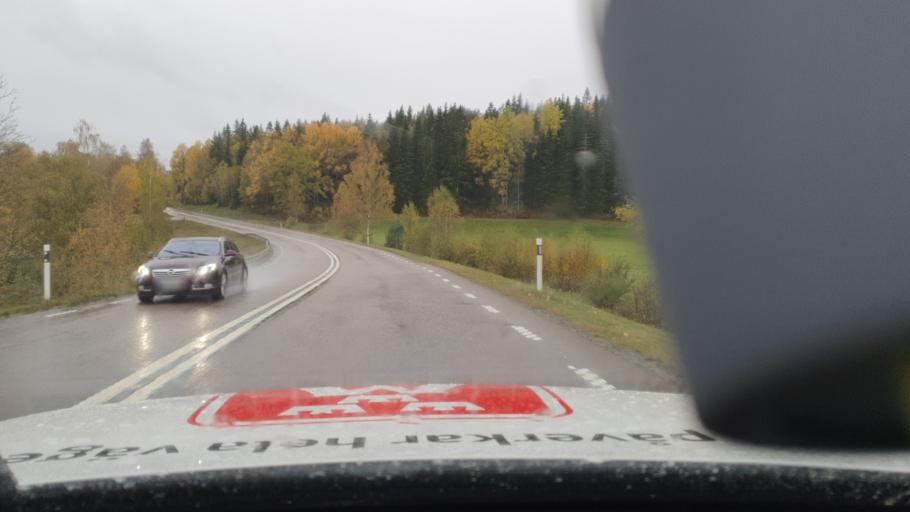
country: SE
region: Vaestra Goetaland
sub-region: Dals-Ed Kommun
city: Ed
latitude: 58.9250
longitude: 12.0334
